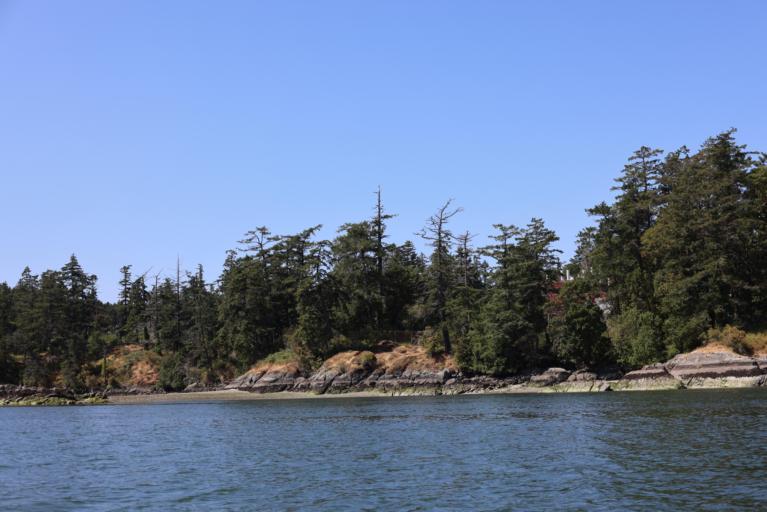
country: CA
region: British Columbia
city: Colwood
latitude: 48.4497
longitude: -123.4484
